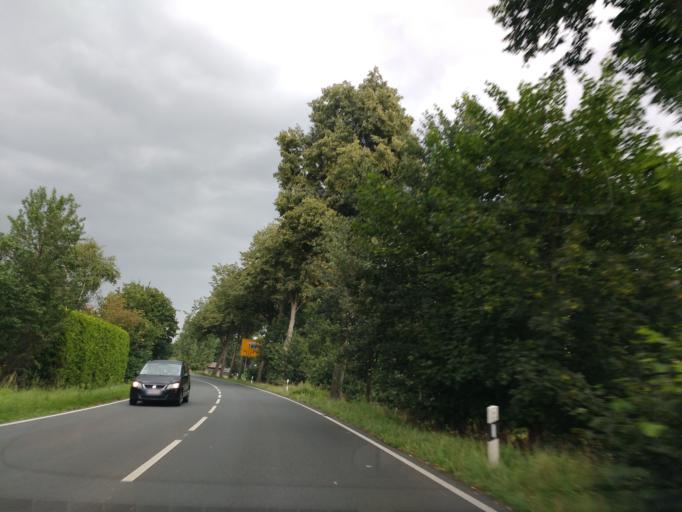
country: DE
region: Lower Saxony
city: Glandorf
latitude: 52.0811
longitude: 8.0064
